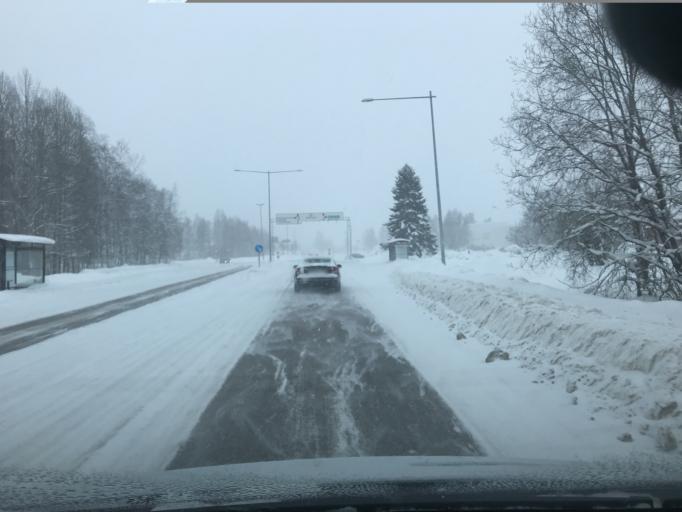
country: SE
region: Norrbotten
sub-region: Lulea Kommun
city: Lulea
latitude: 65.6142
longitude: 22.1331
